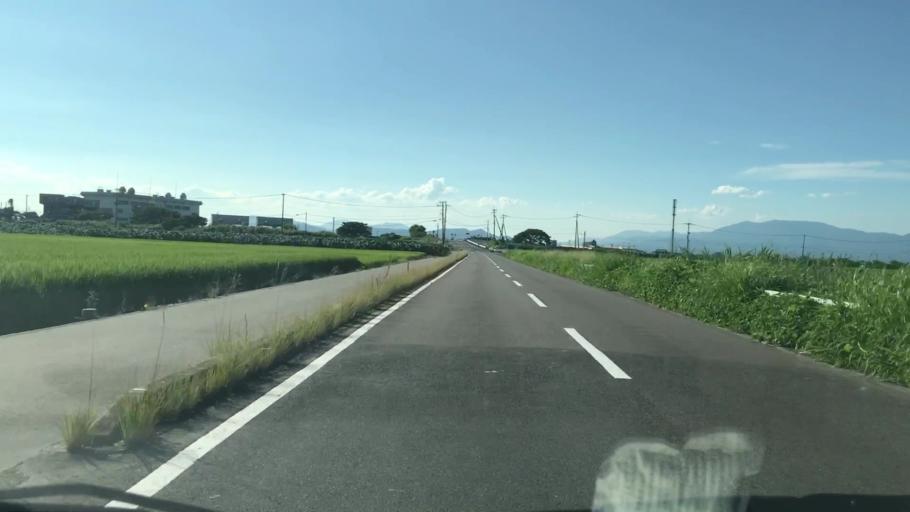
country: JP
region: Saga Prefecture
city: Okawa
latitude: 33.1847
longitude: 130.2943
